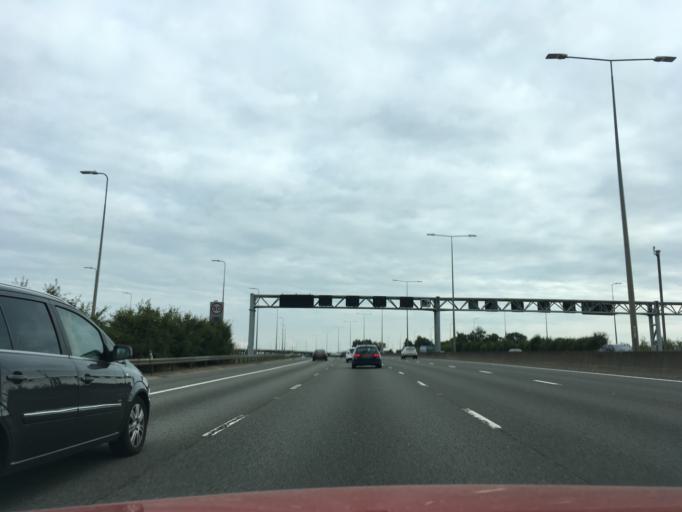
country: GB
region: England
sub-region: Hertfordshire
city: Redbourn
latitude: 51.7618
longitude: -0.4166
